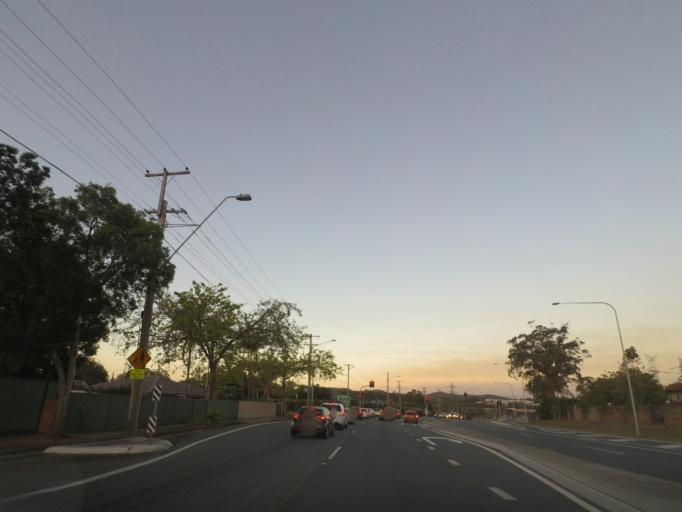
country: AU
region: Queensland
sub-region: Brisbane
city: Mackenzie
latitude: -27.5471
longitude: 153.1103
